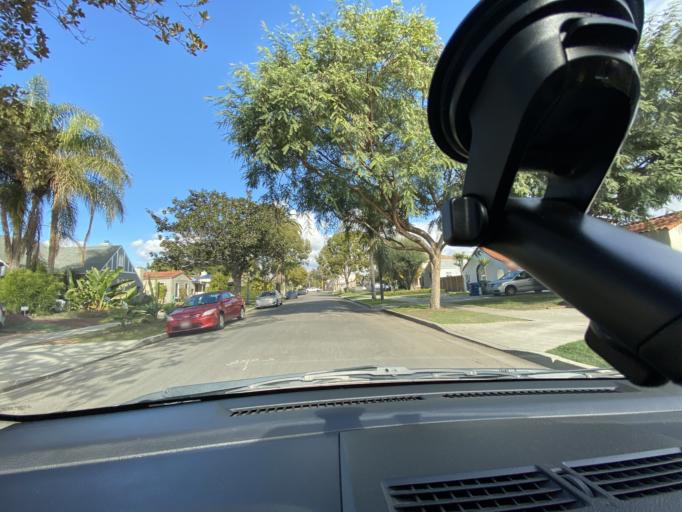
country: US
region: California
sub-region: Los Angeles County
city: Culver City
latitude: 34.0471
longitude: -118.3817
